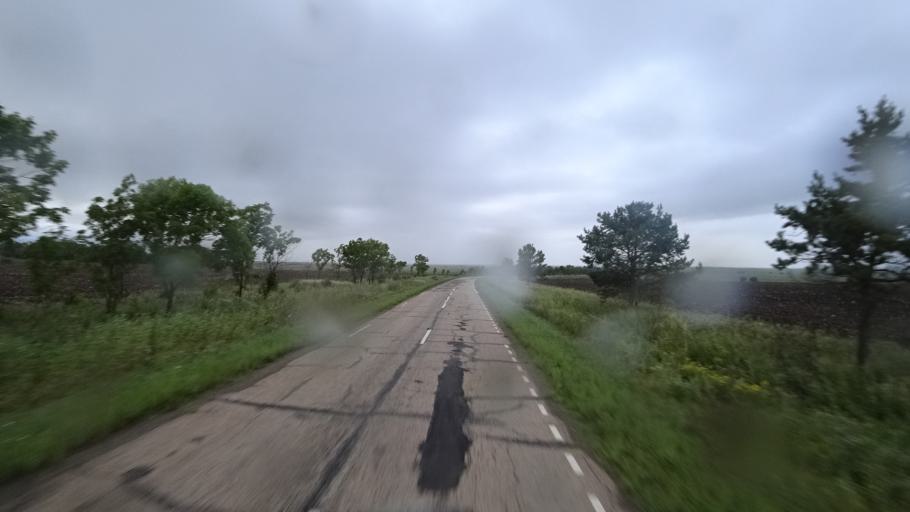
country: RU
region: Primorskiy
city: Chernigovka
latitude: 44.3705
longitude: 132.5309
